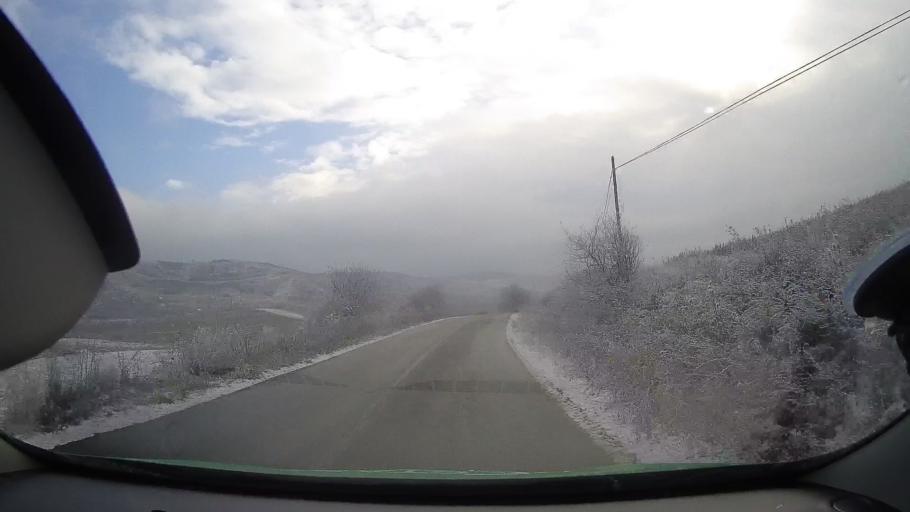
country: RO
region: Mures
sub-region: Comuna Chetani
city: Chetani
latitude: 46.4230
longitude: 24.0151
